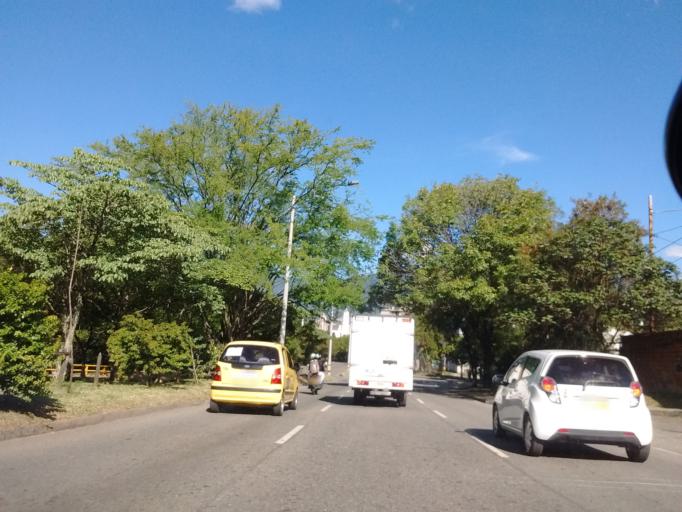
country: CO
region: Antioquia
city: Medellin
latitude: 6.2606
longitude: -75.5838
